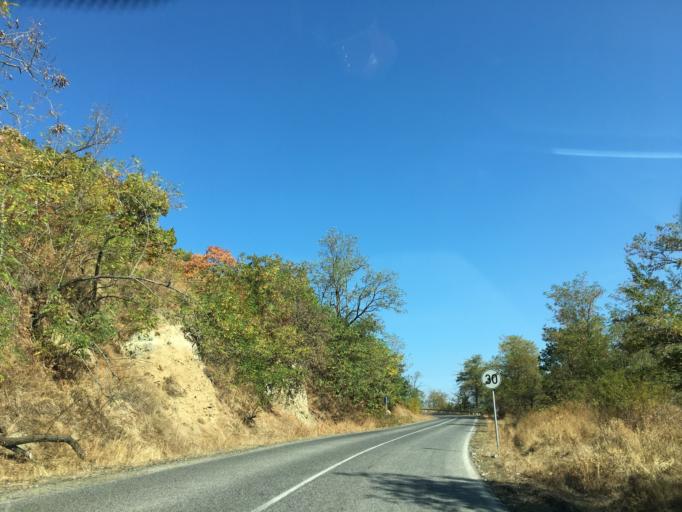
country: BG
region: Kurdzhali
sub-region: Obshtina Krumovgrad
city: Krumovgrad
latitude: 41.4753
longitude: 25.5490
